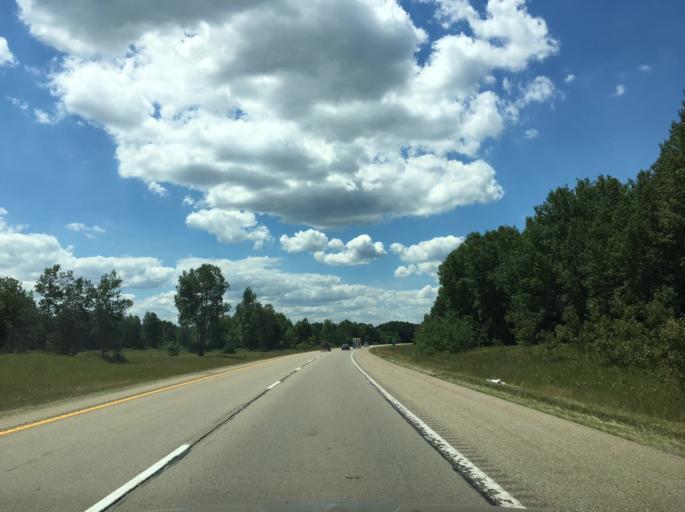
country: US
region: Michigan
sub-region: Clare County
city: Clare
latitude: 43.8777
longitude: -84.8185
